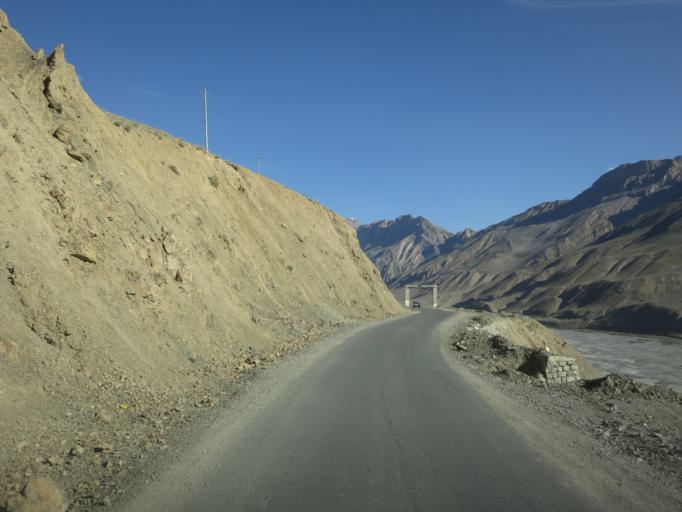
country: IN
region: Himachal Pradesh
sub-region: Shimla
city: Sarahan
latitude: 32.2377
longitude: 78.0608
